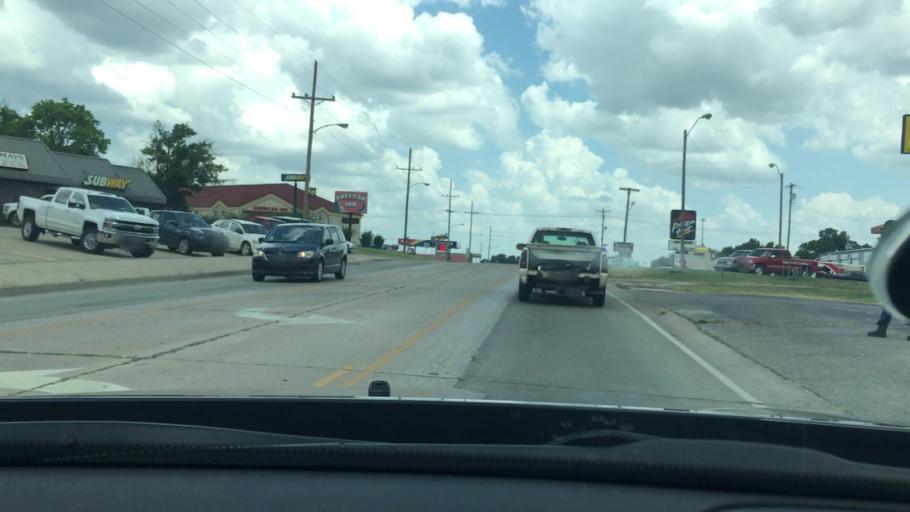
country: US
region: Oklahoma
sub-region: Marshall County
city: Madill
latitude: 34.0957
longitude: -96.7741
